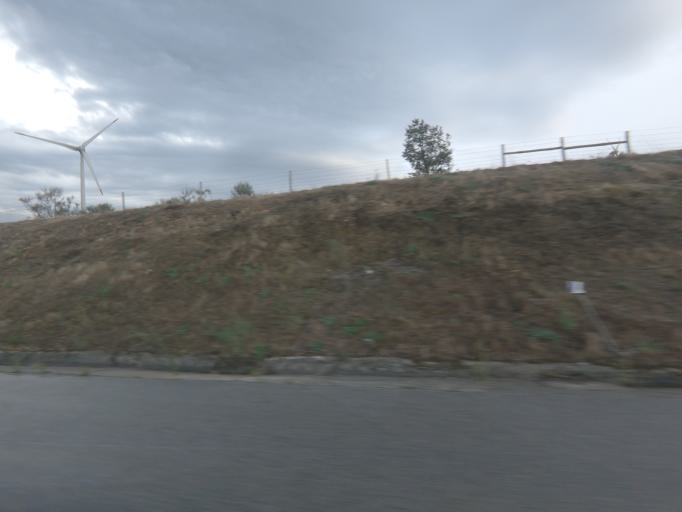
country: PT
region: Viseu
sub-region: Tarouca
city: Tarouca
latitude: 41.0245
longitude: -7.8734
